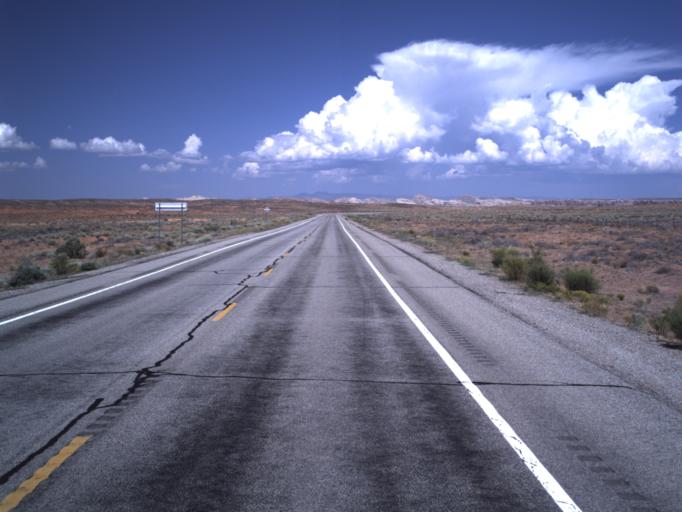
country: US
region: Utah
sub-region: San Juan County
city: Blanding
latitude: 37.2177
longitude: -109.6143
